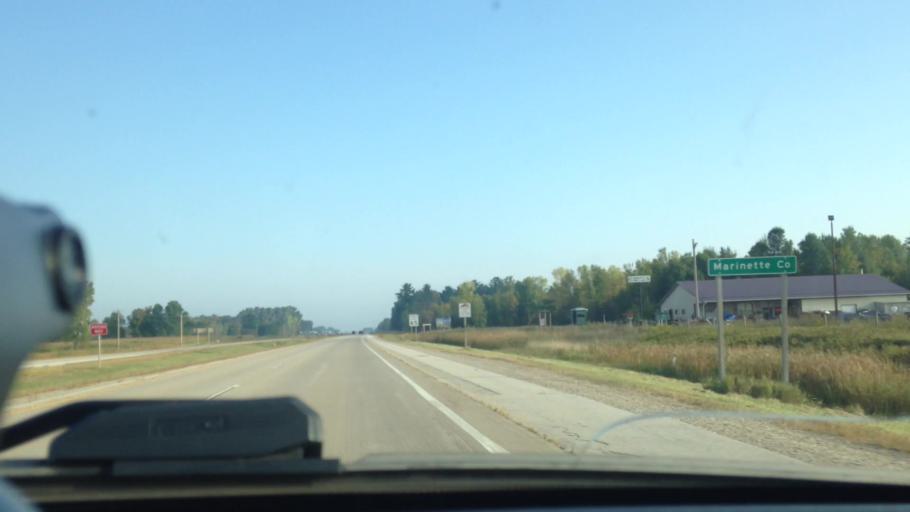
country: US
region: Wisconsin
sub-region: Oconto County
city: Oconto Falls
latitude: 45.0222
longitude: -88.0449
